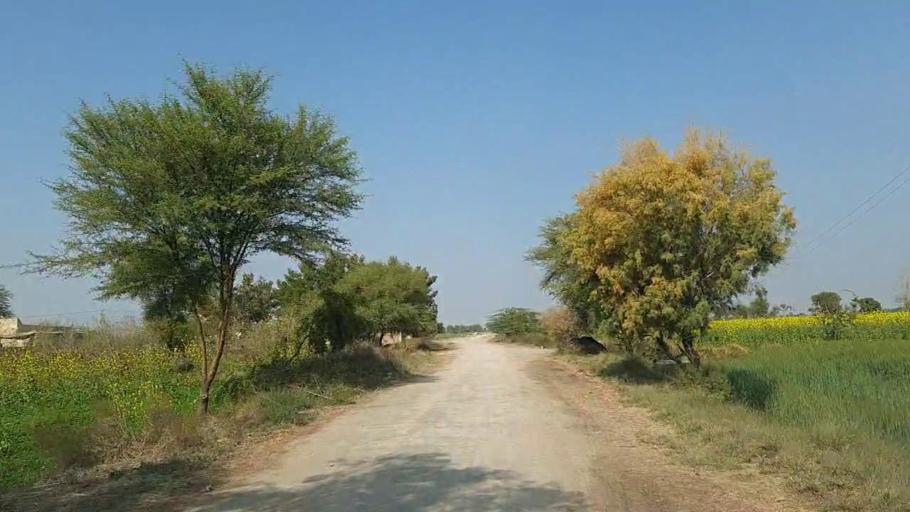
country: PK
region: Sindh
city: Nawabshah
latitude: 26.2910
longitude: 68.5139
